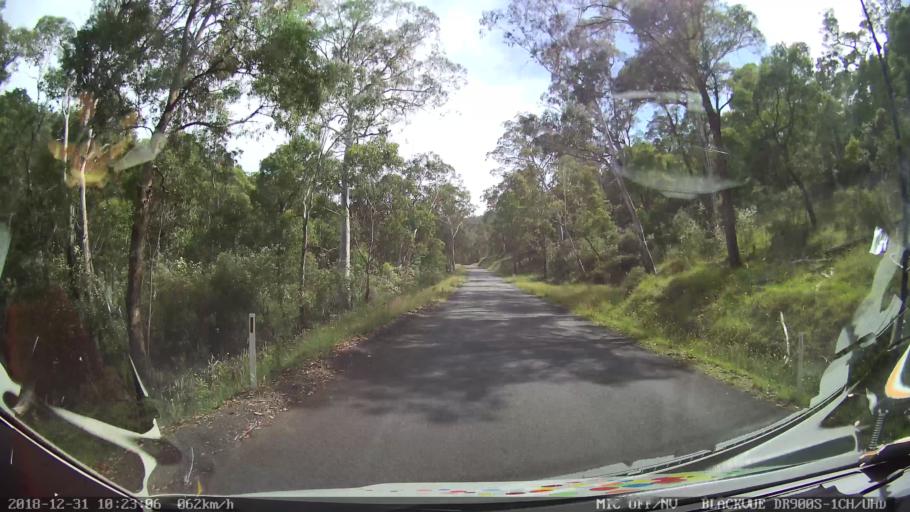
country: AU
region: New South Wales
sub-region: Snowy River
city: Jindabyne
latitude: -36.5198
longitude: 148.1433
